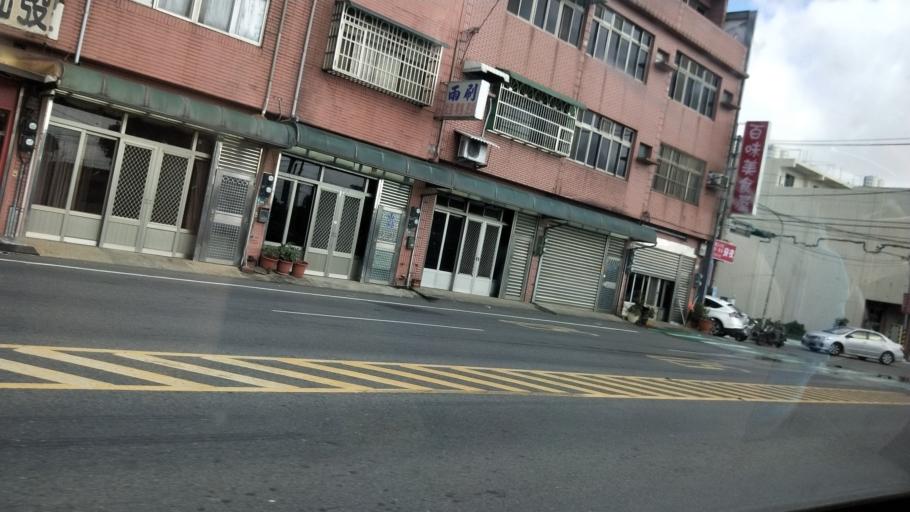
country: TW
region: Taiwan
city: Taoyuan City
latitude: 25.0110
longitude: 121.1363
